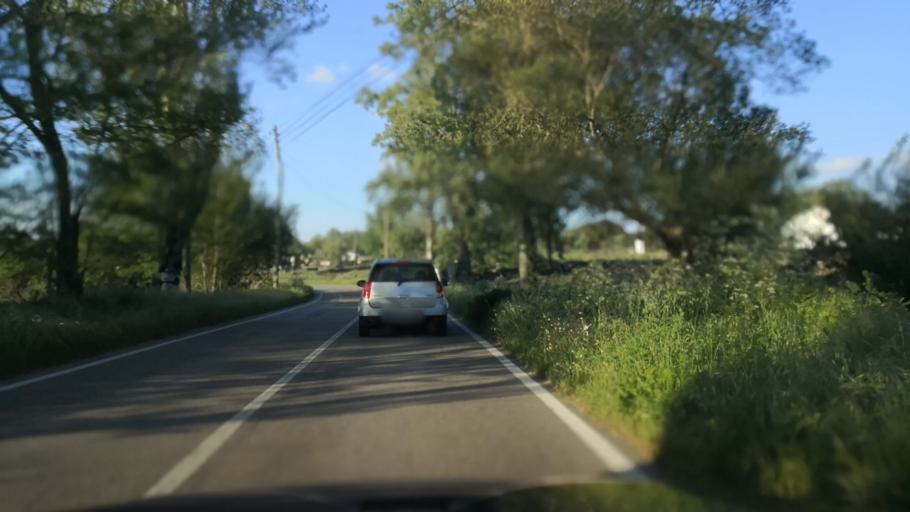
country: PT
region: Portalegre
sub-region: Portalegre
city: Reguengo
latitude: 39.3451
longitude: -7.4083
